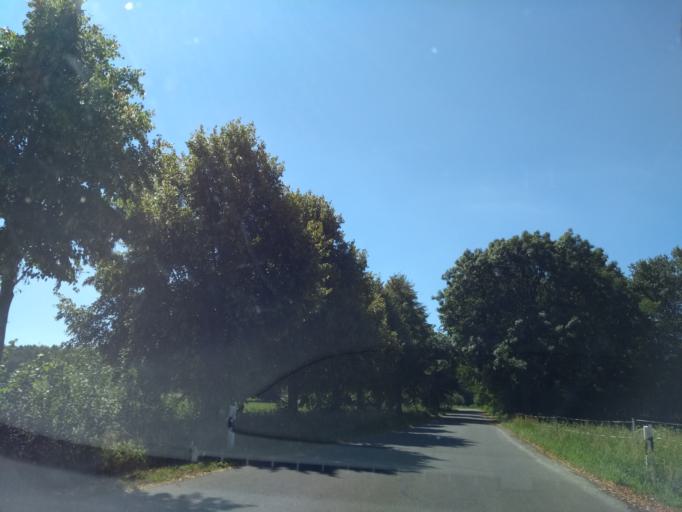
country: DE
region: Brandenburg
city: Lubbenau
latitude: 51.8309
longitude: 13.9533
